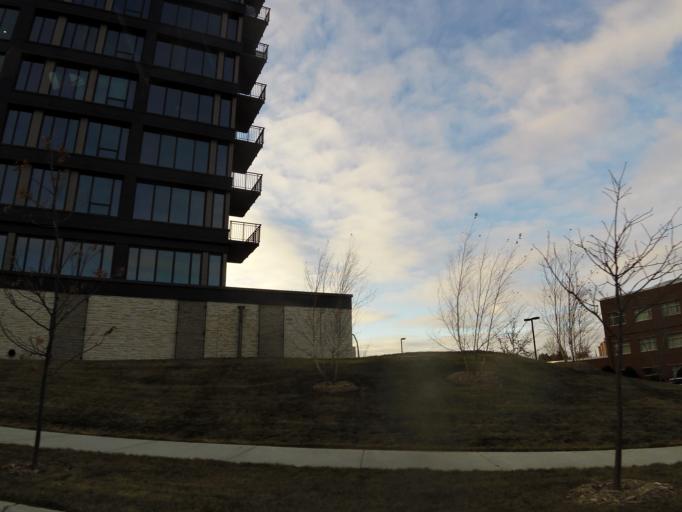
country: US
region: Minnesota
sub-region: Hennepin County
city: Minneapolis
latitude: 44.9767
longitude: -93.2485
